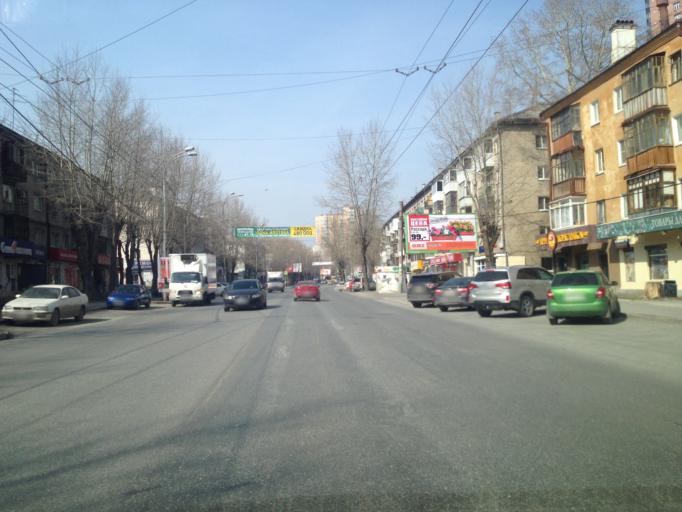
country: RU
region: Sverdlovsk
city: Yekaterinburg
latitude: 56.8037
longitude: 60.6270
